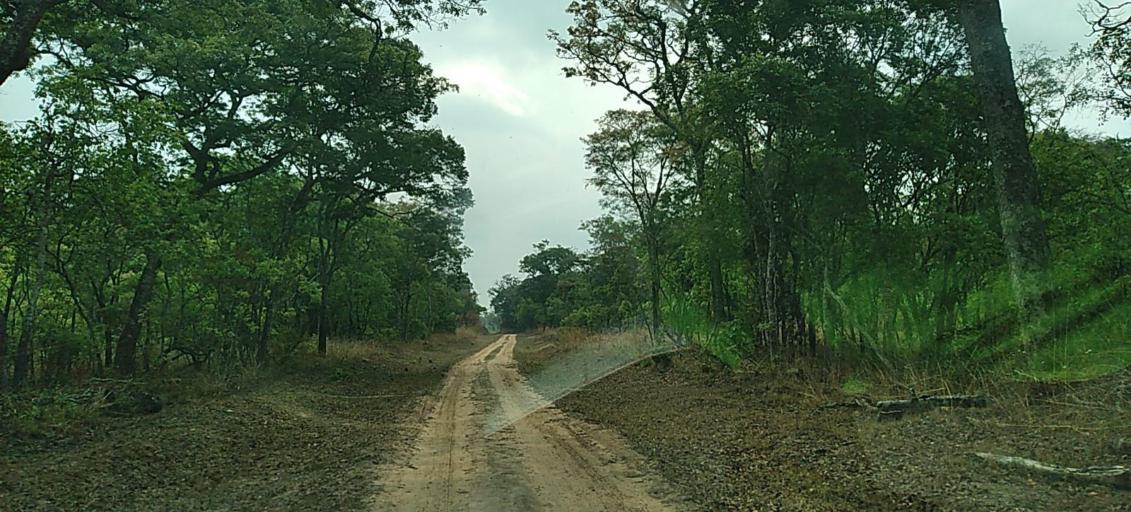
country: ZM
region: North-Western
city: Mwinilunga
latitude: -11.4695
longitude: 24.4822
